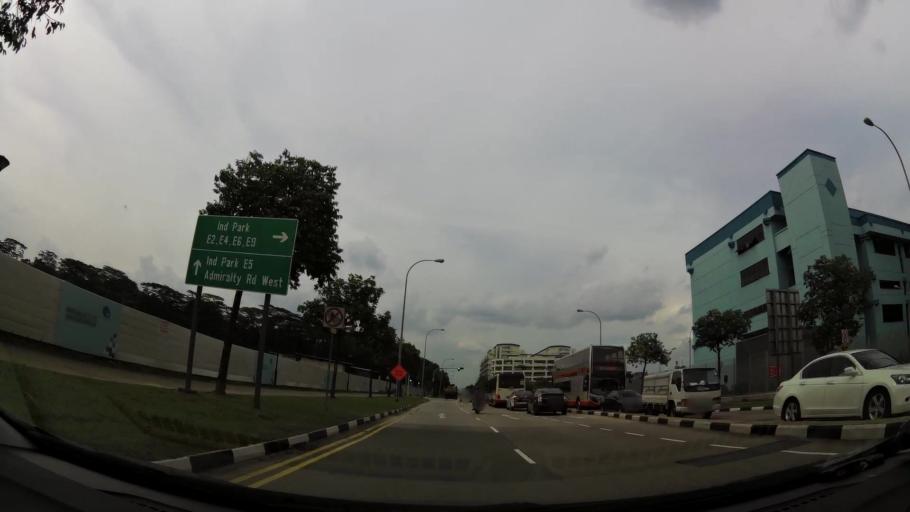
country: MY
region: Johor
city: Johor Bahru
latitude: 1.4466
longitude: 103.7922
